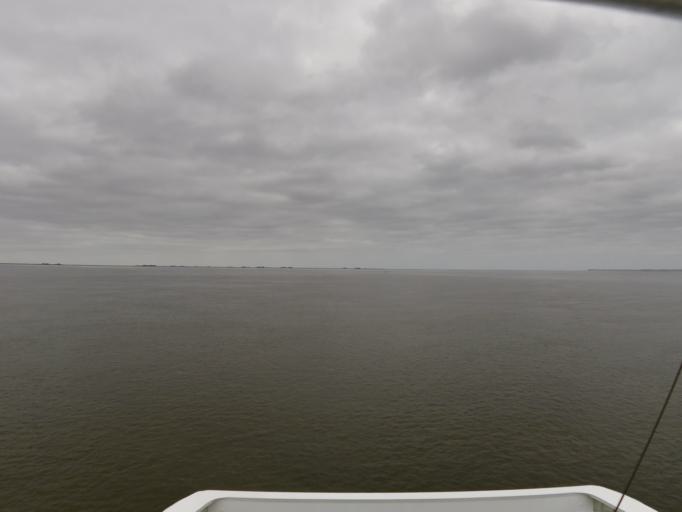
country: DE
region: Schleswig-Holstein
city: Wyk auf Fohr
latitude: 54.6848
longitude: 8.6151
